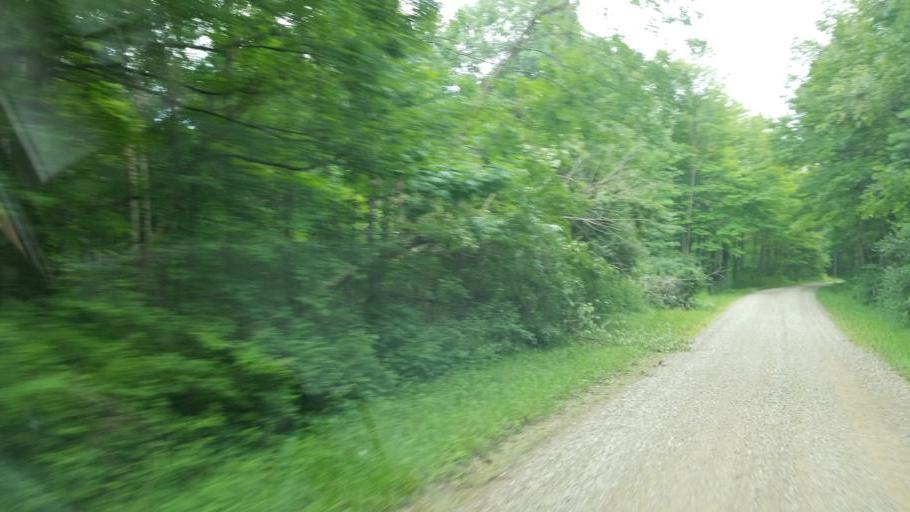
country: US
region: Ohio
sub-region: Knox County
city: Fredericktown
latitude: 40.4899
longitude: -82.6594
